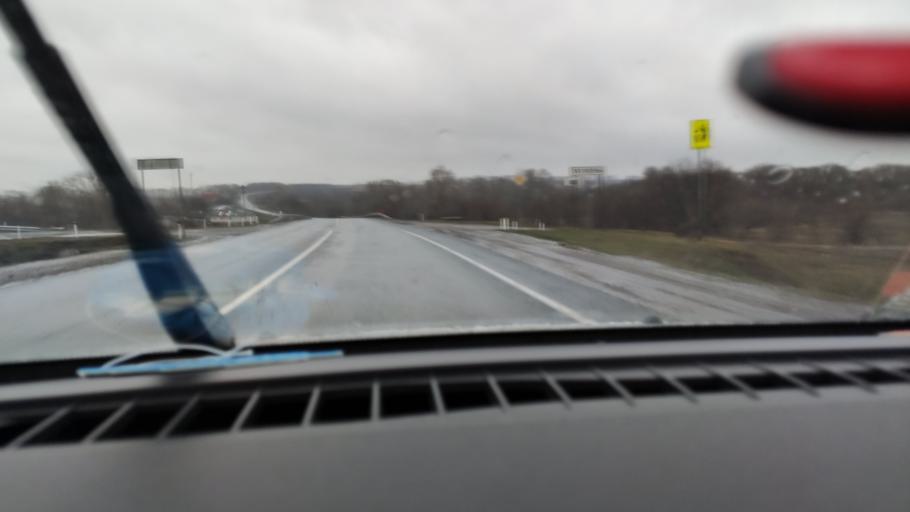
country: RU
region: Tatarstan
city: Mendeleyevsk
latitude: 55.8598
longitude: 52.2124
